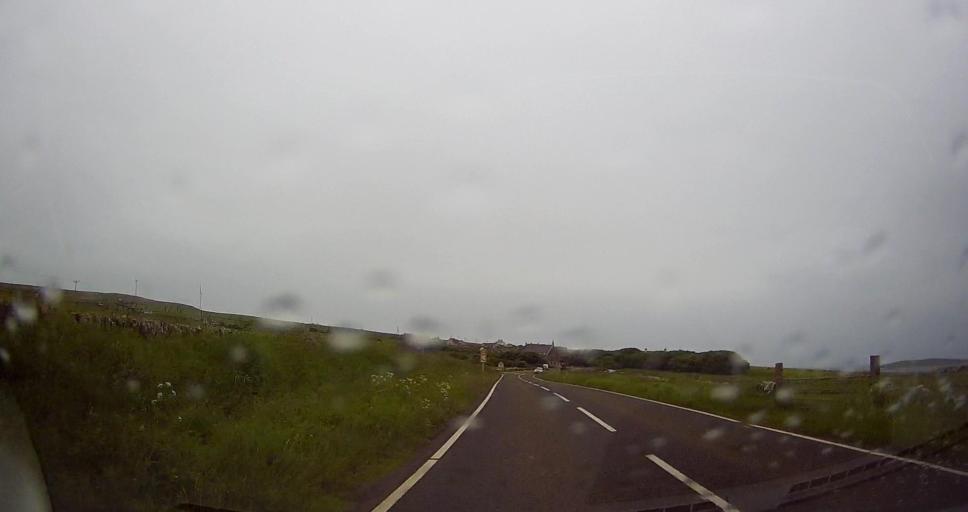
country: GB
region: Scotland
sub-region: Orkney Islands
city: Orkney
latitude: 59.1109
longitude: -3.1009
